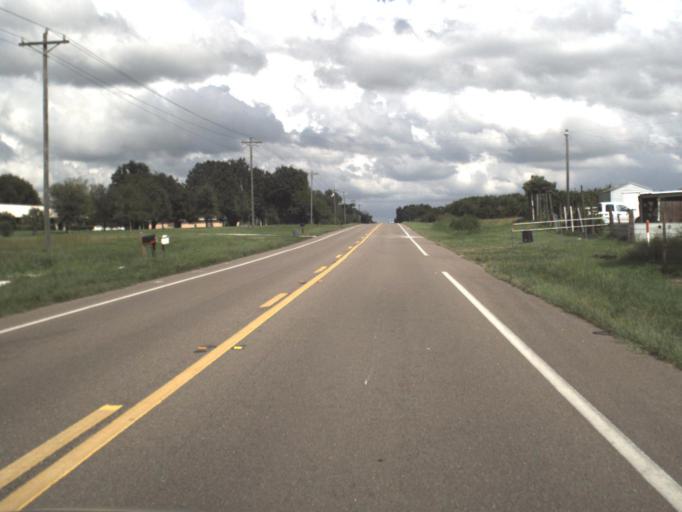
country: US
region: Florida
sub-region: Hardee County
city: Zolfo Springs
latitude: 27.4917
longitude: -81.8366
